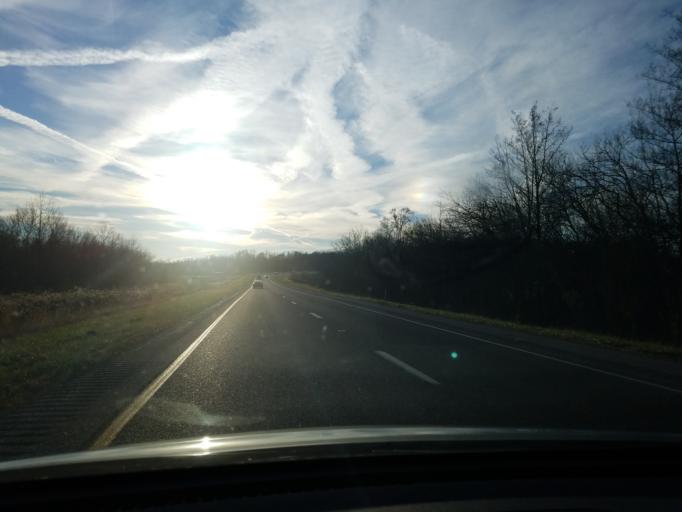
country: US
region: Indiana
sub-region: Dubois County
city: Ferdinand
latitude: 38.2084
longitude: -86.7798
